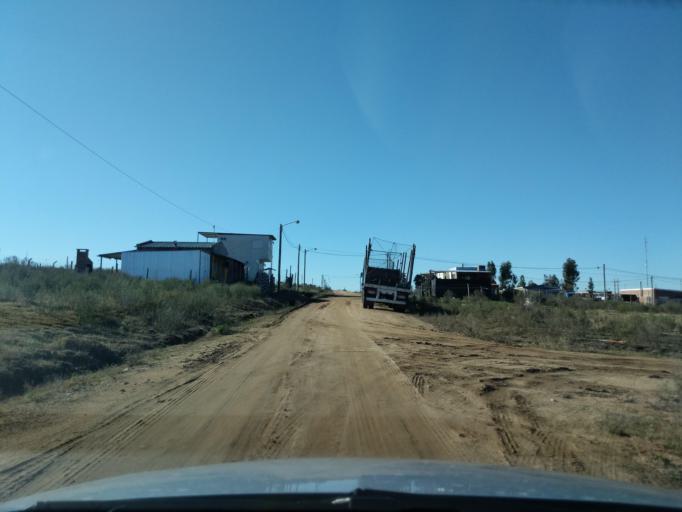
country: UY
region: Florida
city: Florida
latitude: -34.0804
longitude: -56.2387
